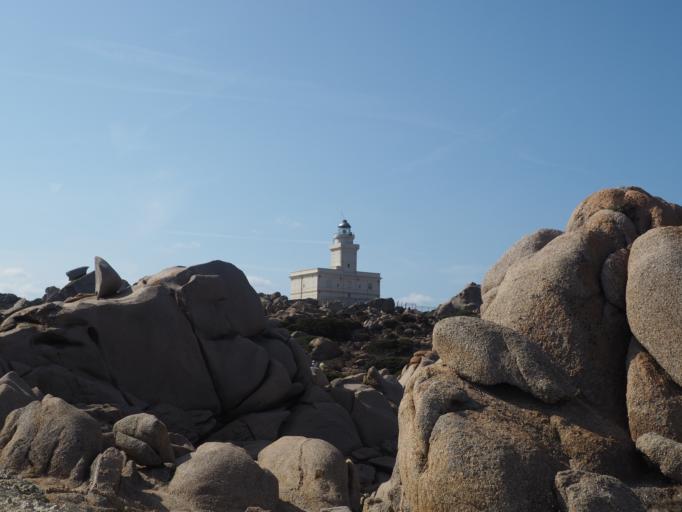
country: IT
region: Sardinia
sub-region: Provincia di Olbia-Tempio
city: Santa Teresa Gallura
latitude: 41.2457
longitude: 9.1449
